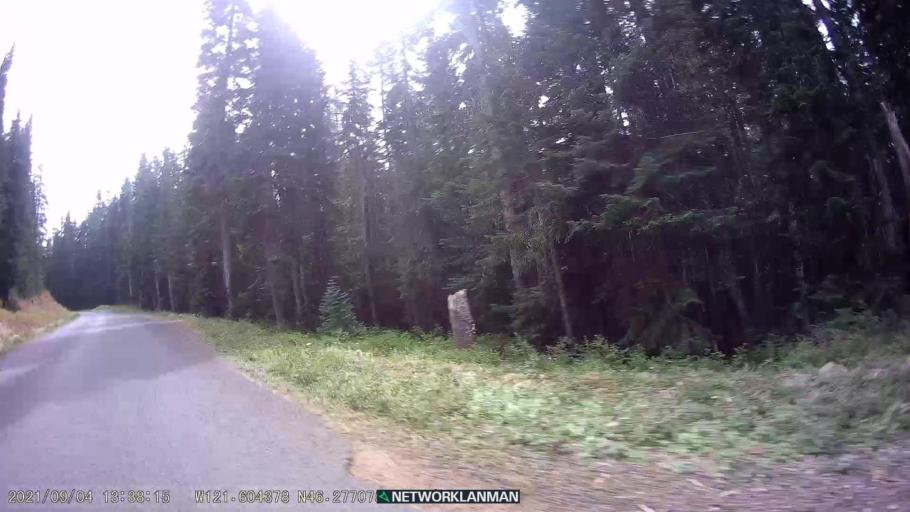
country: US
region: Washington
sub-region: Klickitat County
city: White Salmon
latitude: 46.2771
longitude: -121.6046
